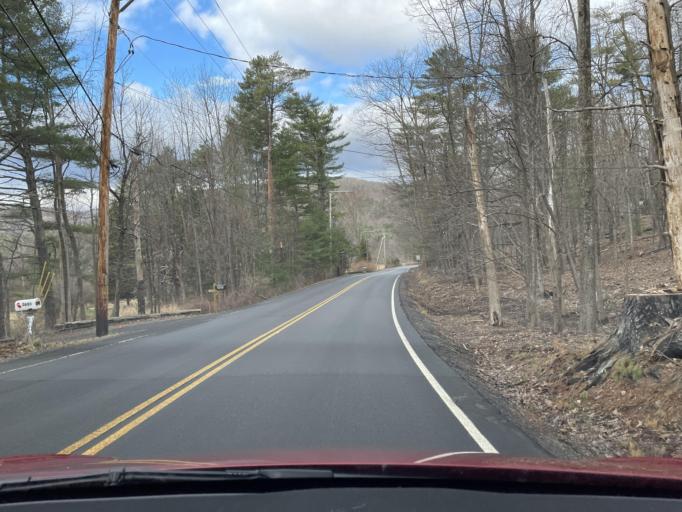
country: US
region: New York
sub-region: Ulster County
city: Woodstock
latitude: 42.0526
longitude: -74.1538
